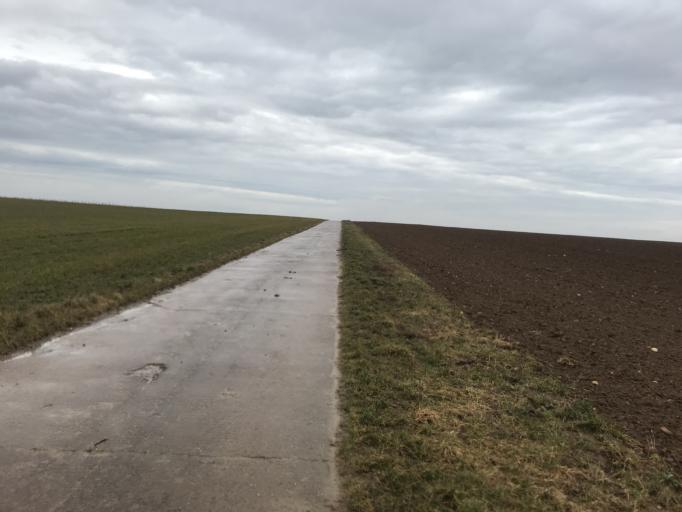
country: DE
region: Rheinland-Pfalz
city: Essenheim
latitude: 49.9385
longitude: 8.1582
